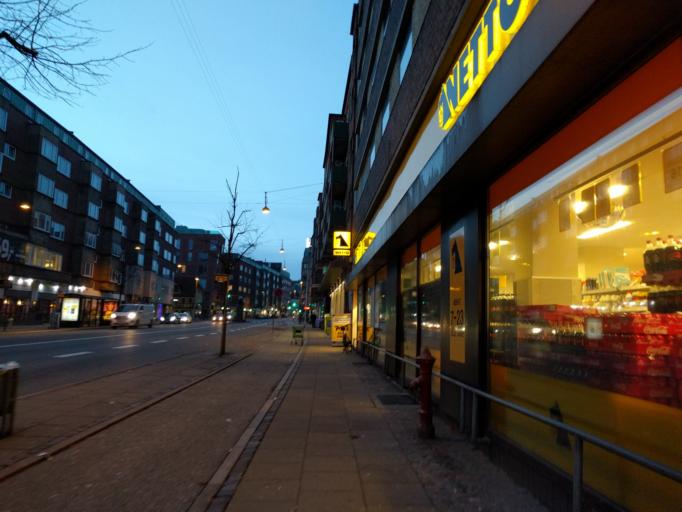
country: DK
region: North Denmark
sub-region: Alborg Kommune
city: Aalborg
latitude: 57.0504
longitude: 9.9164
